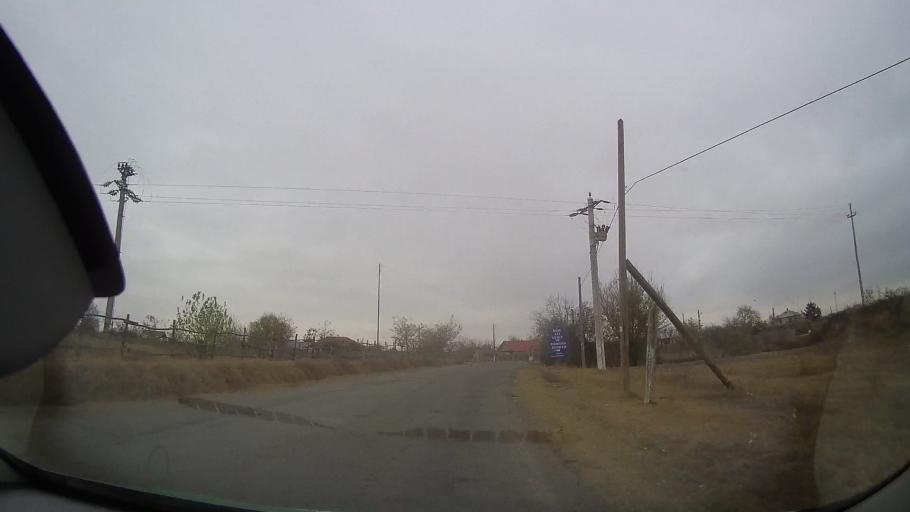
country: RO
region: Buzau
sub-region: Comuna Rusetu
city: Rusetu
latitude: 44.9534
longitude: 27.2182
